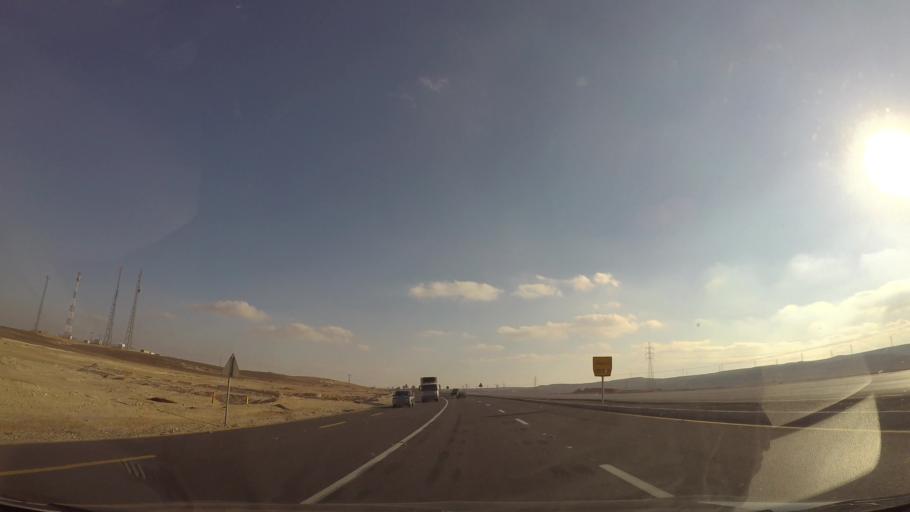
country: JO
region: Karak
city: Karak City
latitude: 31.1128
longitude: 36.0070
